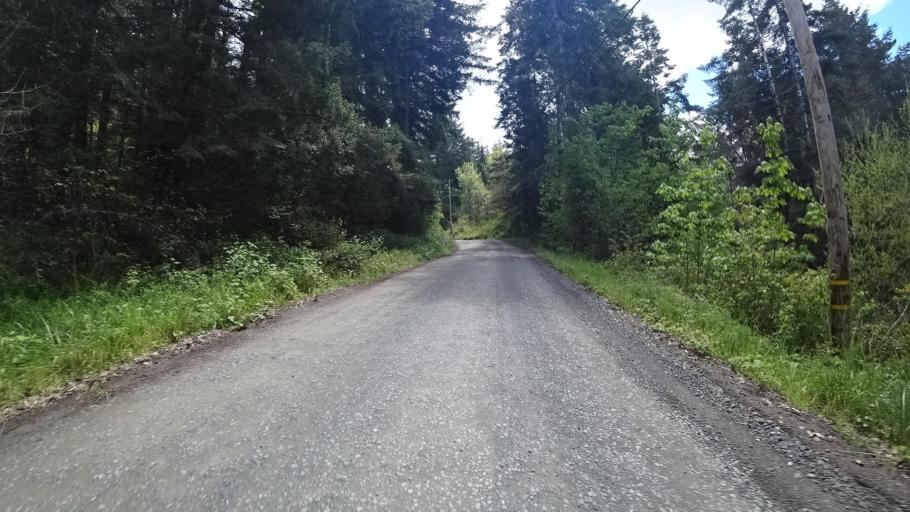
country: US
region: California
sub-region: Humboldt County
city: Blue Lake
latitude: 40.7709
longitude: -123.8760
